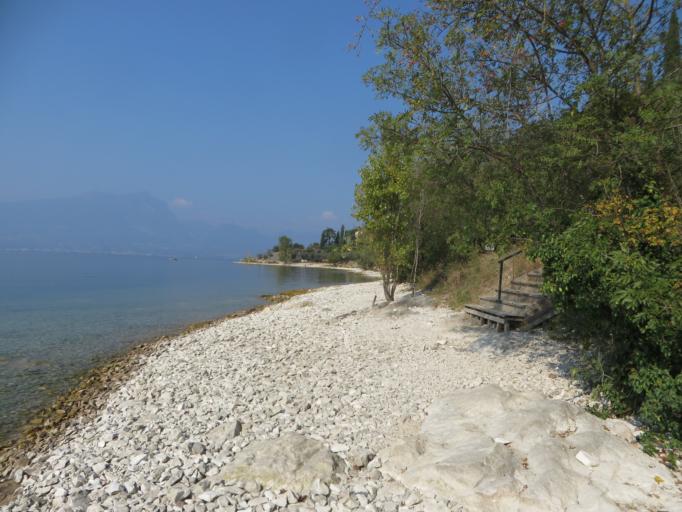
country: IT
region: Veneto
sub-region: Provincia di Verona
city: Torri del Benaco
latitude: 45.5754
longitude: 10.6736
